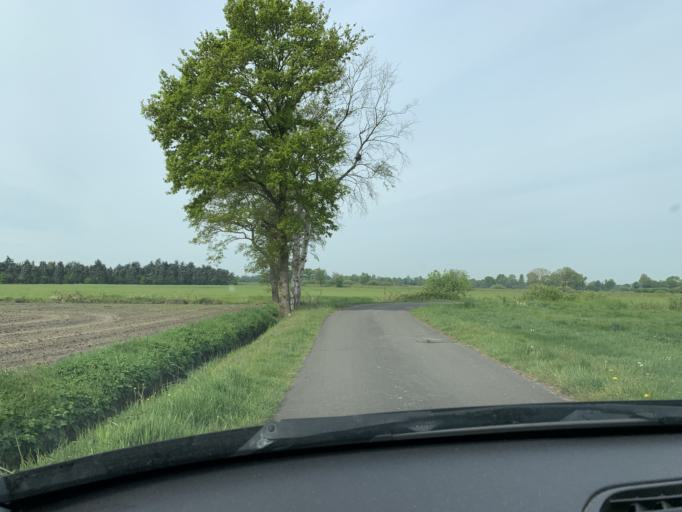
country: DE
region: Lower Saxony
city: Apen
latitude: 53.2377
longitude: 7.8326
